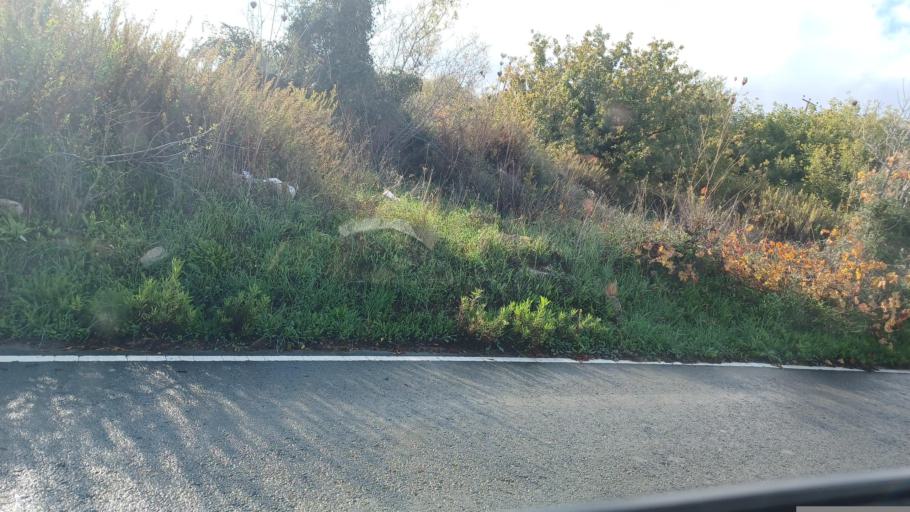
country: CY
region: Pafos
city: Mesogi
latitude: 34.8435
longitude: 32.5331
